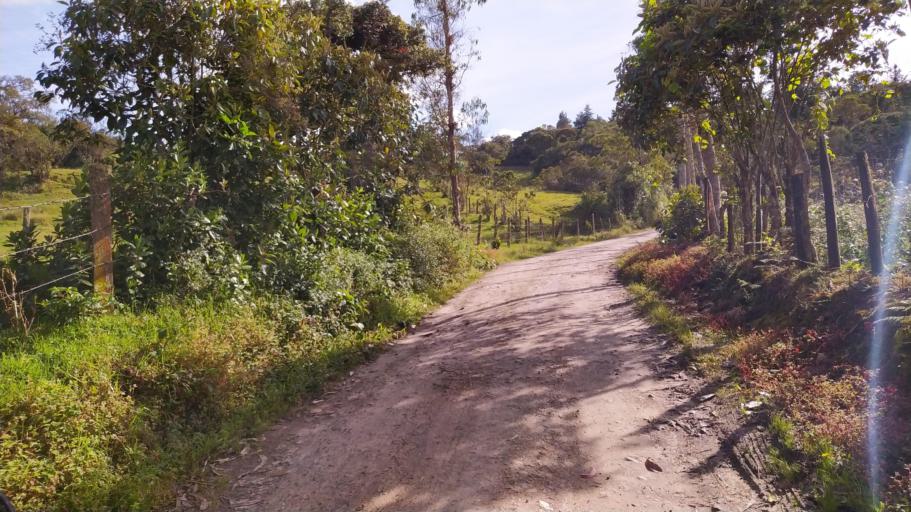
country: CO
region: Cundinamarca
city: Tenza
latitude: 5.0873
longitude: -73.4814
